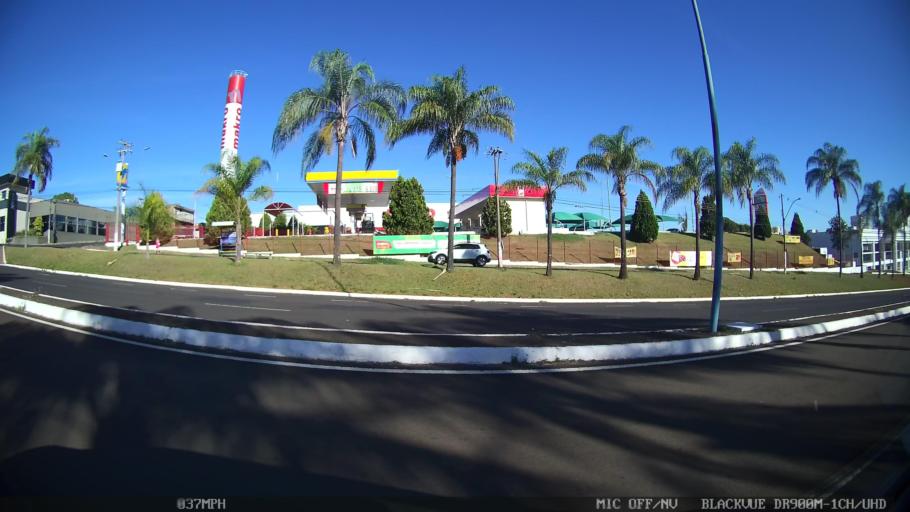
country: BR
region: Sao Paulo
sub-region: Franca
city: Franca
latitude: -20.5544
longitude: -47.3962
